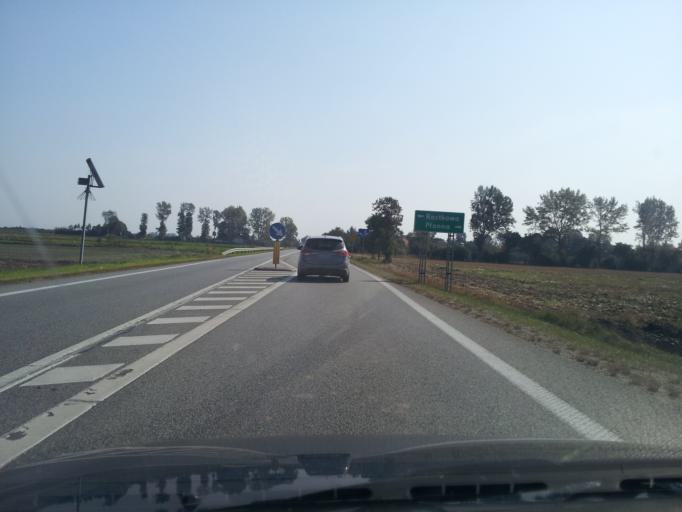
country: PL
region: Masovian Voivodeship
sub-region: Powiat plonski
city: Dzierzaznia
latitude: 52.6400
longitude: 20.1346
